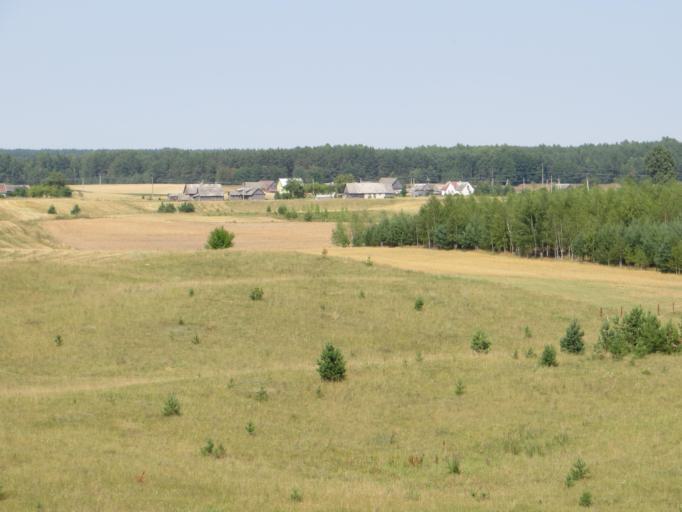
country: LT
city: Veisiejai
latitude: 54.1014
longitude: 23.7221
